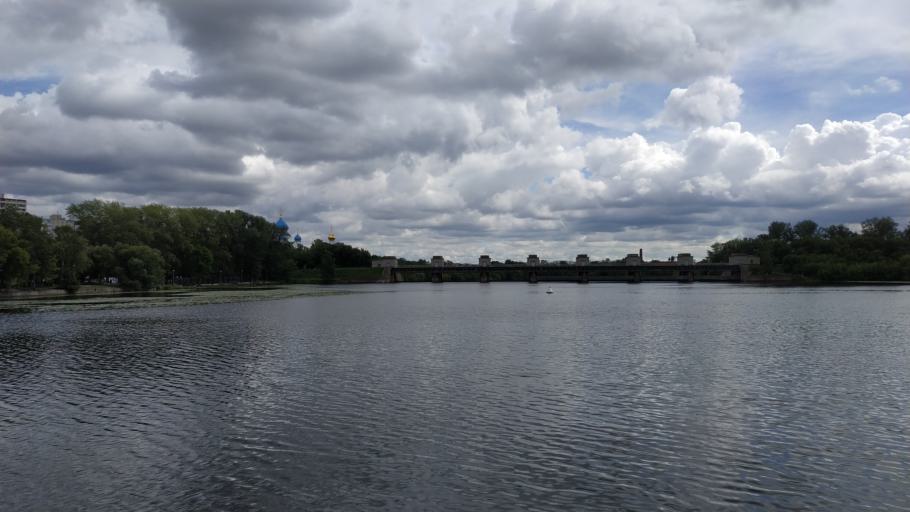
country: RU
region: Moscow
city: Mar'ino
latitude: 55.6752
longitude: 37.7138
